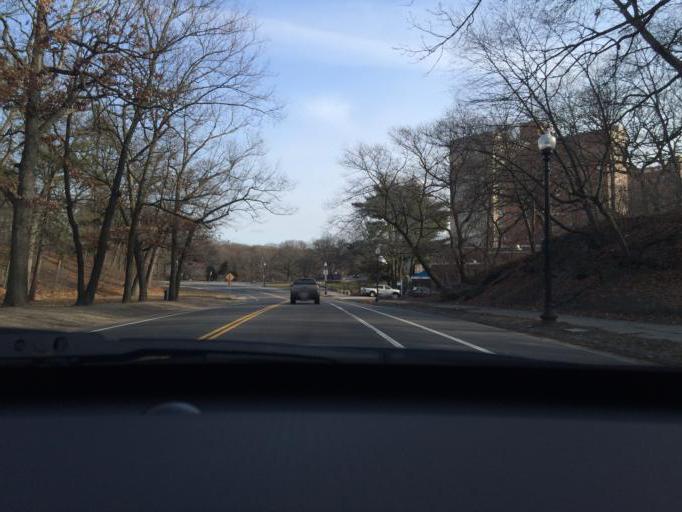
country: US
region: Massachusetts
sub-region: Suffolk County
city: Jamaica Plain
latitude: 42.3011
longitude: -71.1040
